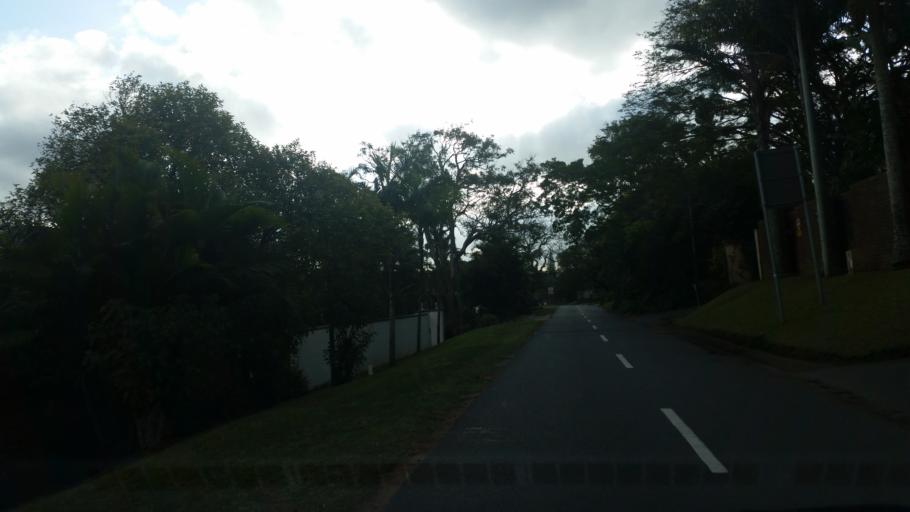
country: ZA
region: KwaZulu-Natal
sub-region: eThekwini Metropolitan Municipality
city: Berea
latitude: -29.8313
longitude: 30.9346
